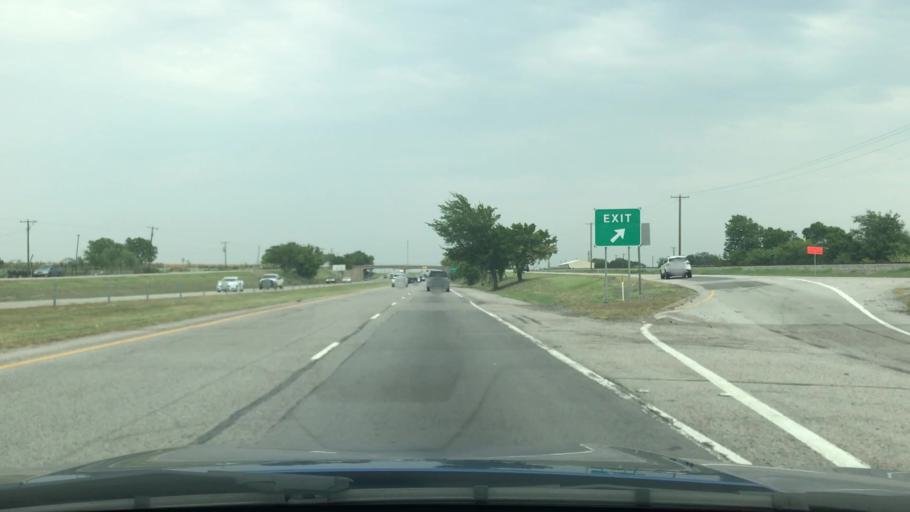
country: US
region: Texas
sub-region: Kaufman County
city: Forney
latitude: 32.7410
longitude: -96.4338
